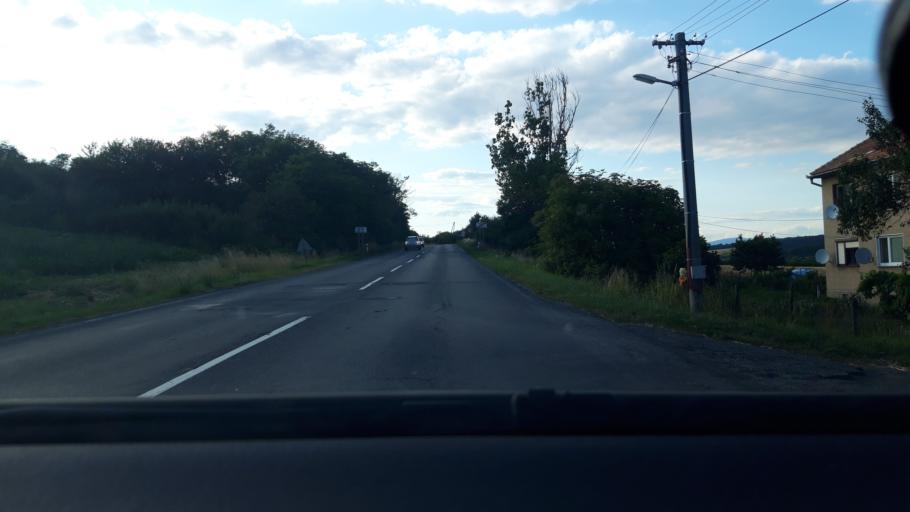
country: SK
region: Banskobystricky
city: Lucenec
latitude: 48.3242
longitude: 19.6979
